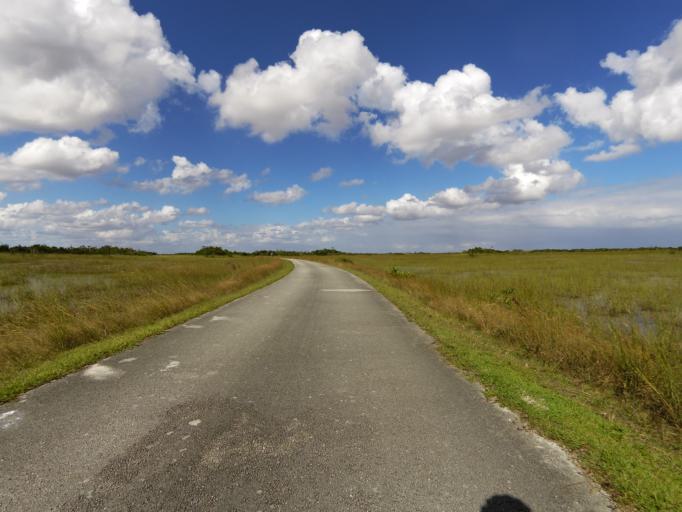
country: US
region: Florida
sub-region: Miami-Dade County
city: The Hammocks
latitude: 25.7085
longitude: -80.7614
